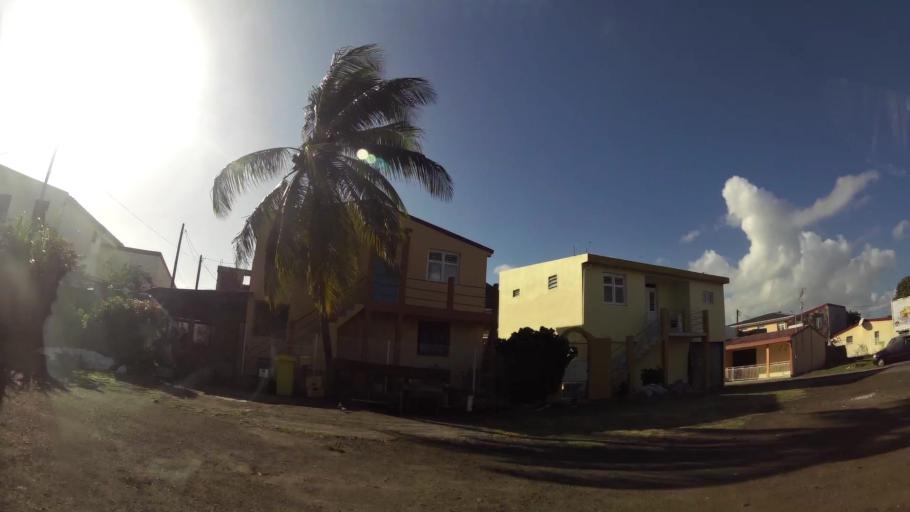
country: MQ
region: Martinique
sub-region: Martinique
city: Le Francois
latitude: 14.6169
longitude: -60.9048
